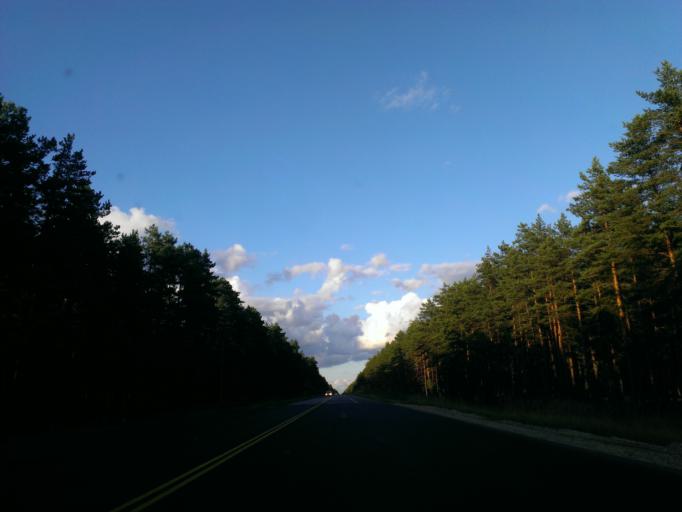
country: LV
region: Garkalne
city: Garkalne
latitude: 57.0610
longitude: 24.4655
